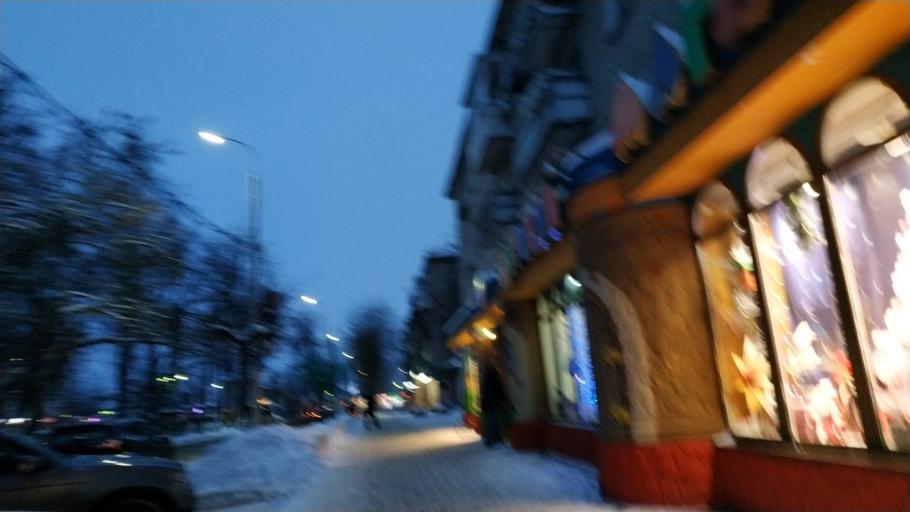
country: RU
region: Moskovskaya
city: Shchelkovo
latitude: 55.9206
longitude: 37.9751
